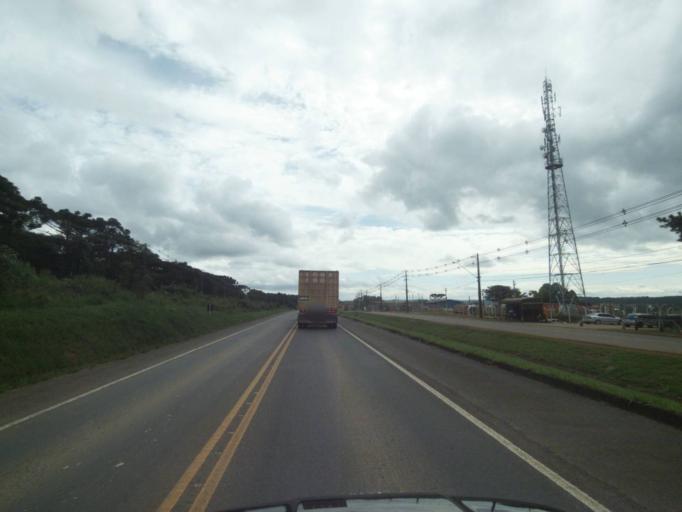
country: BR
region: Parana
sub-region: Telemaco Borba
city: Telemaco Borba
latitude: -24.3766
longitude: -50.6665
